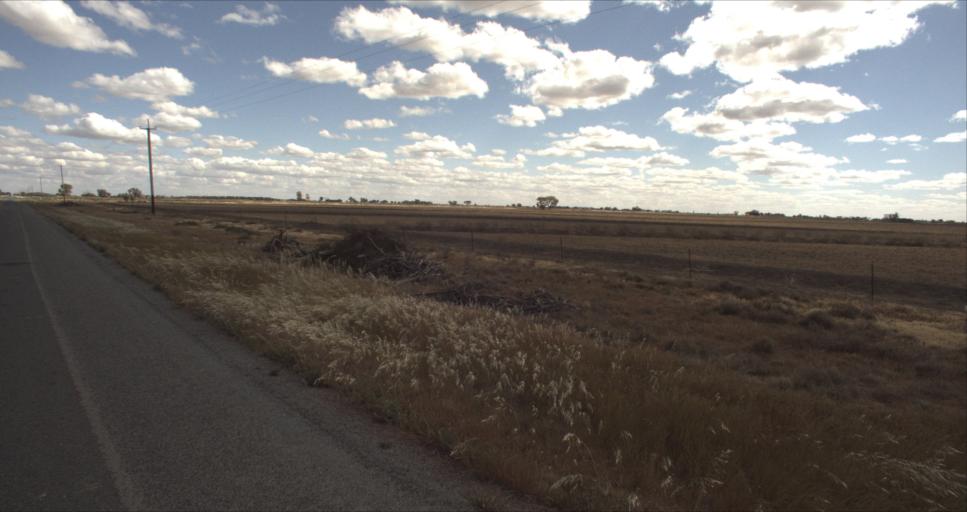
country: AU
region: New South Wales
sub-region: Leeton
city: Leeton
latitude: -34.4419
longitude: 146.2562
